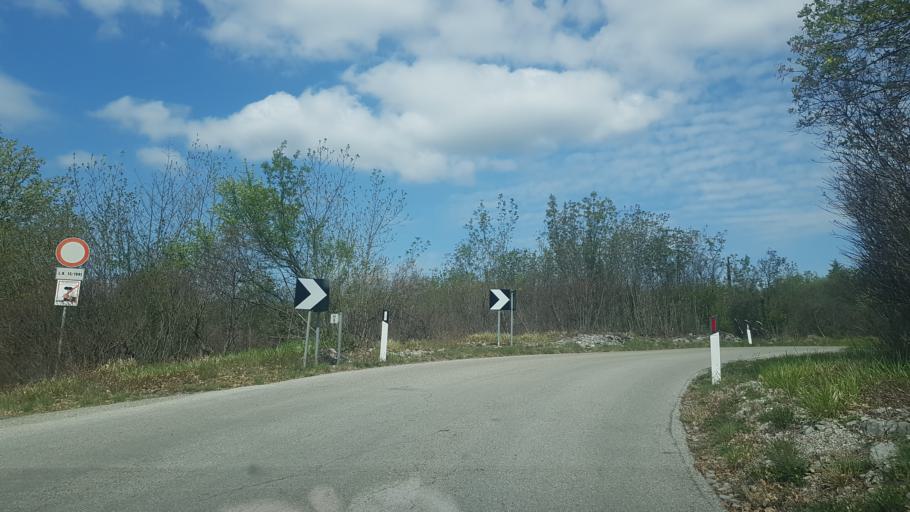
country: IT
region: Friuli Venezia Giulia
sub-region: Provincia di Gorizia
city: Doberdo del Lago
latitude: 45.8682
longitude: 13.5412
